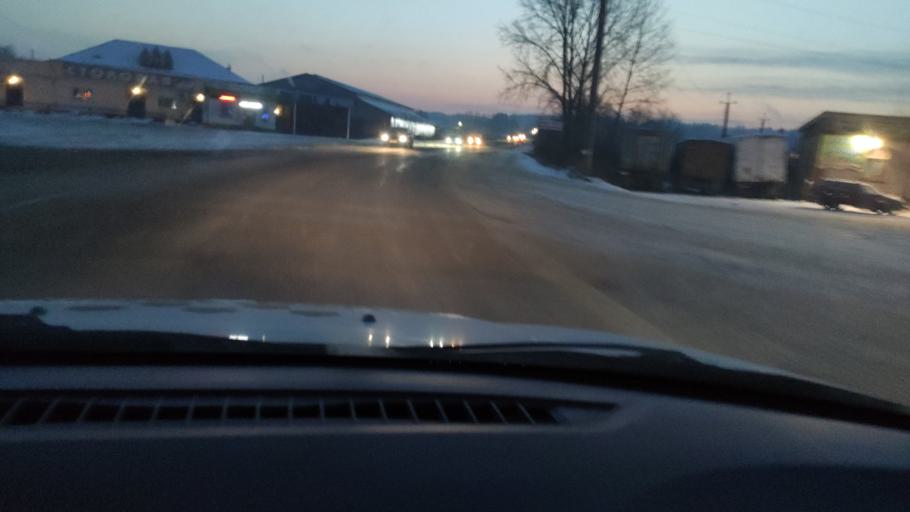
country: RU
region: Perm
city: Kungur
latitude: 57.4255
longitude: 56.9316
